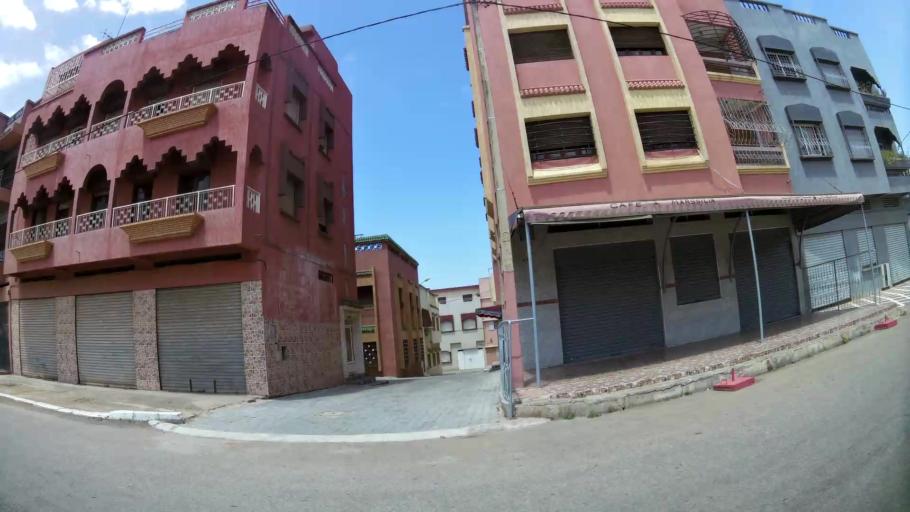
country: MA
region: Gharb-Chrarda-Beni Hssen
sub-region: Kenitra Province
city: Kenitra
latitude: 34.2697
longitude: -6.6006
